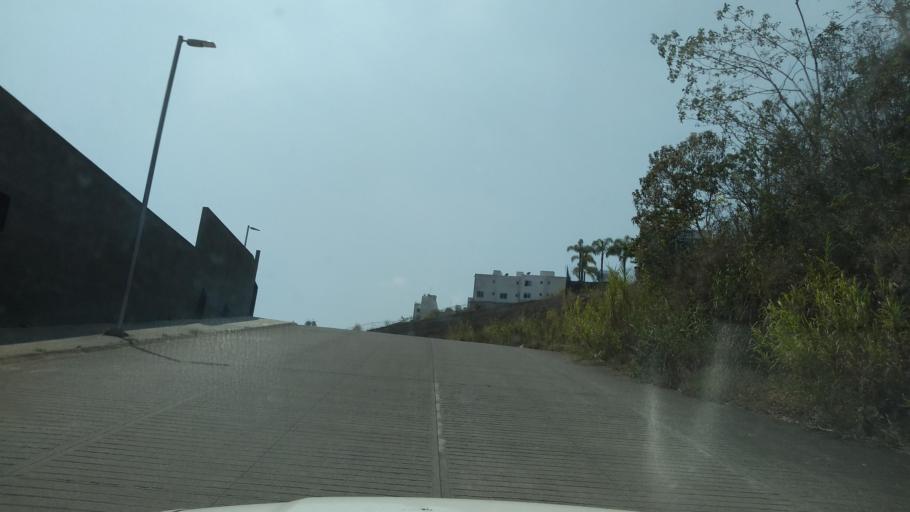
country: MX
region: Veracruz
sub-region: Emiliano Zapata
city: Las Trancas
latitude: 19.5135
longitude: -96.8603
